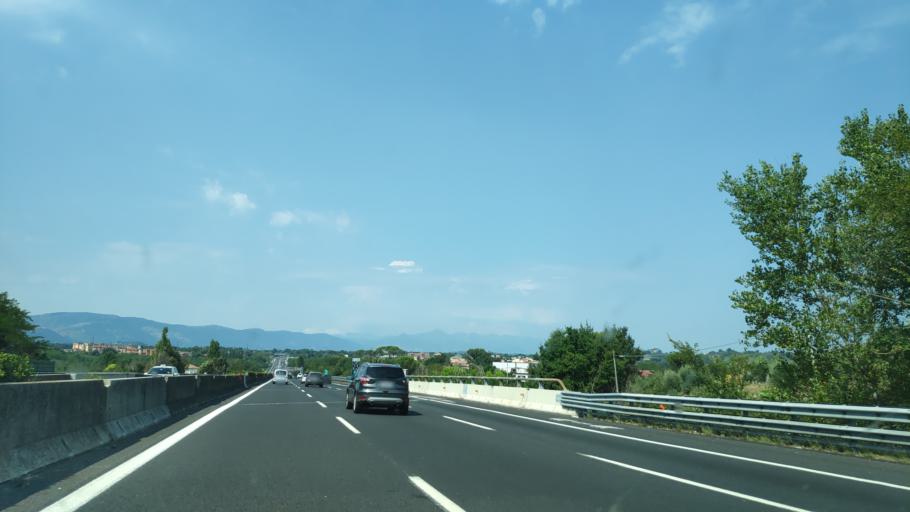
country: IT
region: Latium
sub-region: Provincia di Frosinone
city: Ceprano
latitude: 41.5434
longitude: 13.5295
